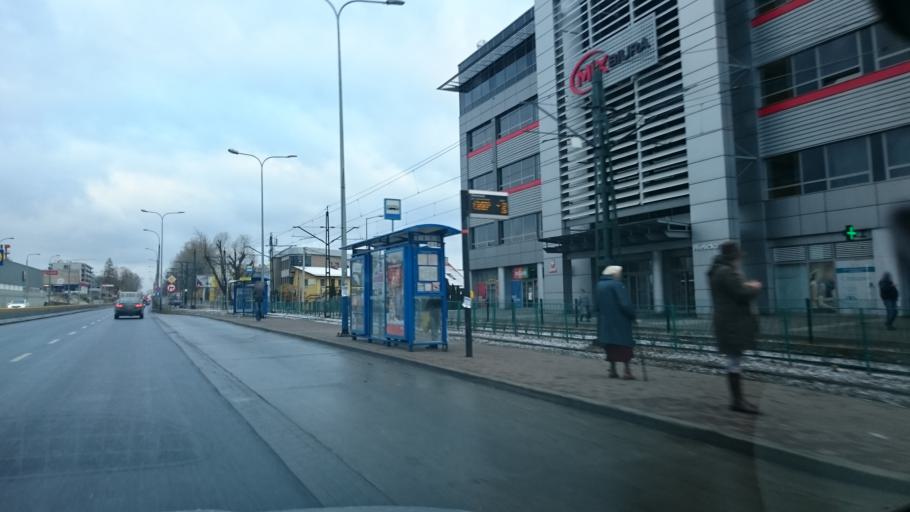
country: PL
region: Lesser Poland Voivodeship
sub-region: Krakow
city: Krakow
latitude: 50.0333
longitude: 19.9704
